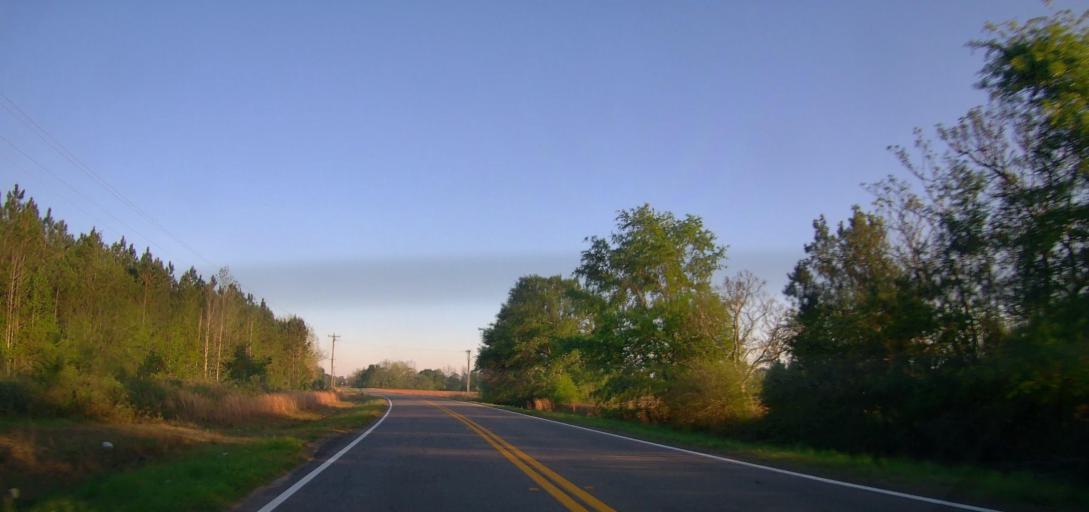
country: US
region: Georgia
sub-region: Irwin County
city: Ocilla
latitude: 31.6140
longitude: -83.2644
